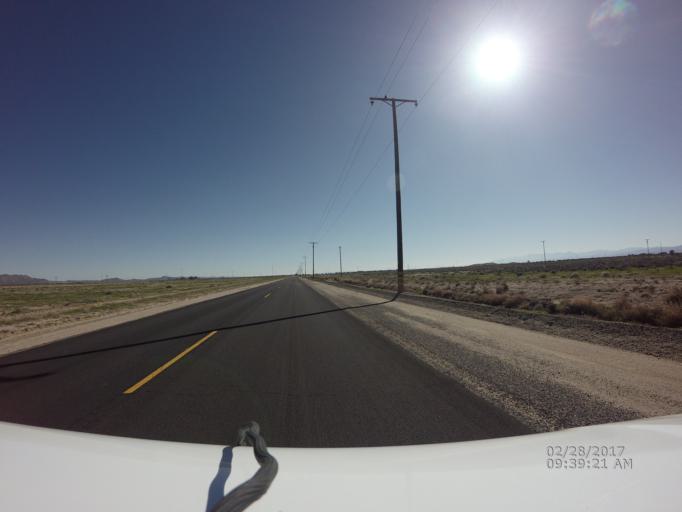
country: US
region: California
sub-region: Kern County
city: Rosamond
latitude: 34.8195
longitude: -118.3384
